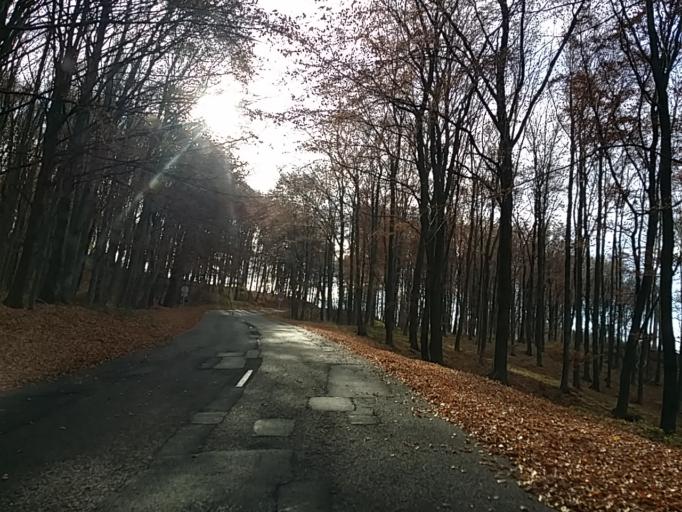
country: HU
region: Heves
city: Paradsasvar
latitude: 47.8708
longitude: 19.9879
